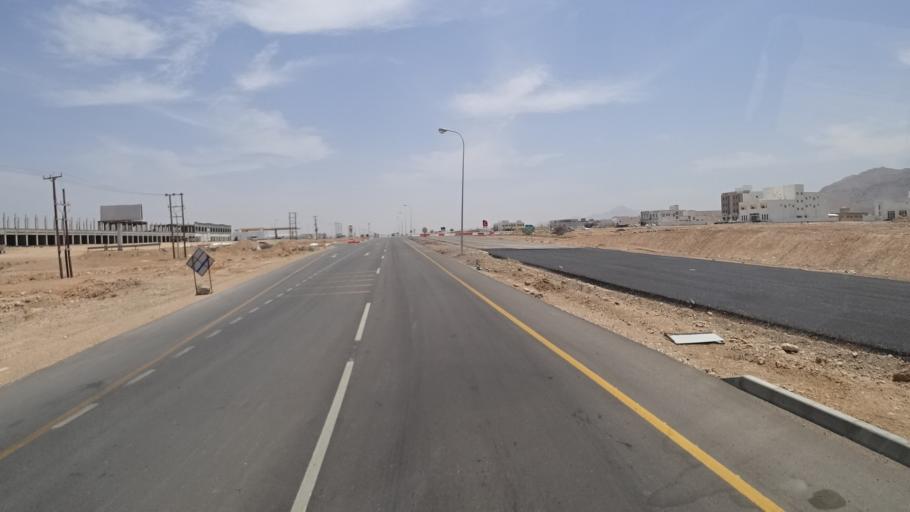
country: OM
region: Ash Sharqiyah
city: Sur
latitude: 22.6040
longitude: 59.4307
